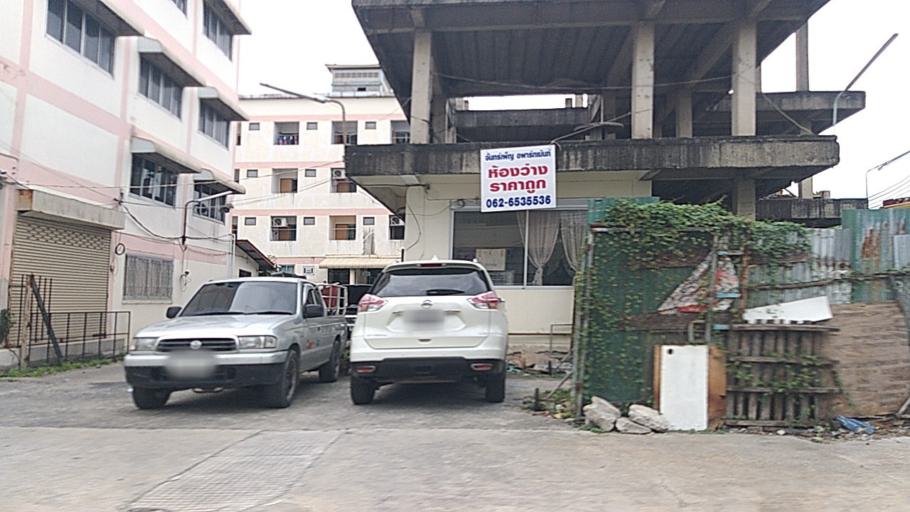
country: TH
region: Bangkok
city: Bang Na
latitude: 13.6746
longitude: 100.6797
